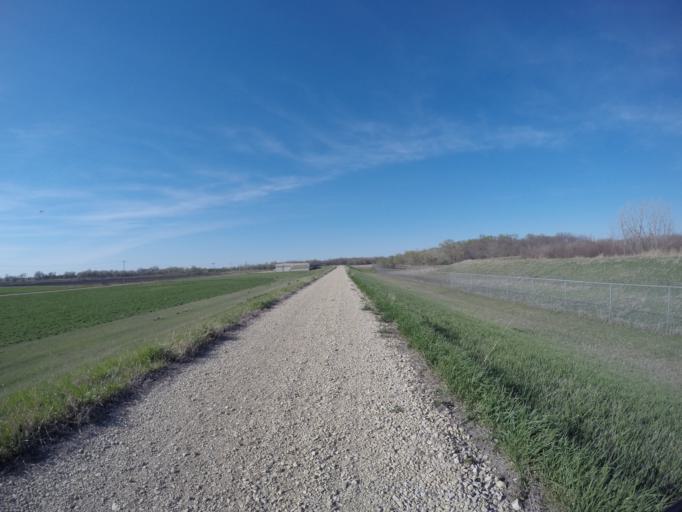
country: US
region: Kansas
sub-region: Saline County
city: Salina
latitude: 38.8552
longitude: -97.5748
